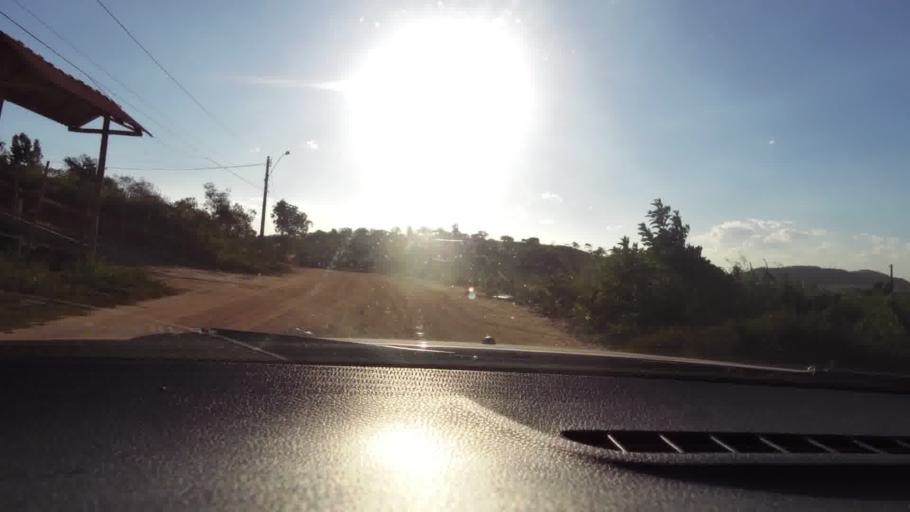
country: BR
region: Espirito Santo
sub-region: Guarapari
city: Guarapari
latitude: -20.5528
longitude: -40.4159
